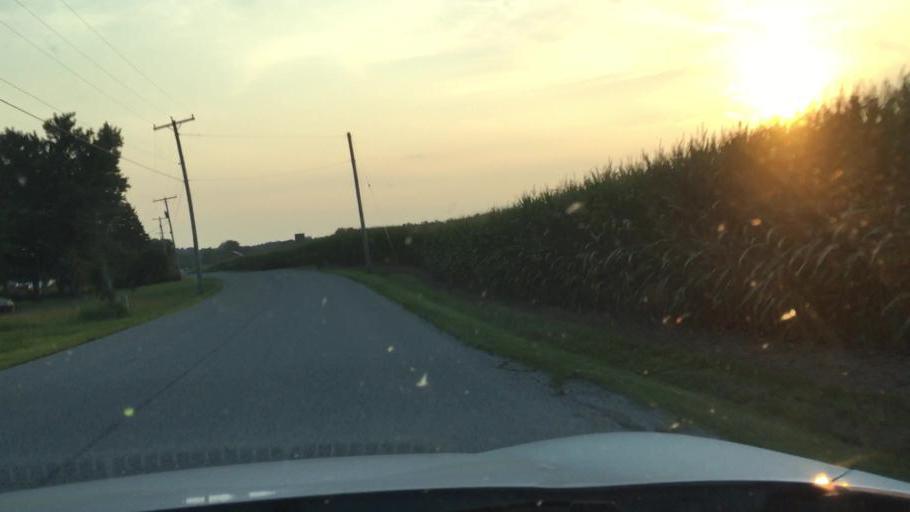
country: US
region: Ohio
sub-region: Madison County
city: Choctaw Lake
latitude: 39.9474
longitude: -83.5781
